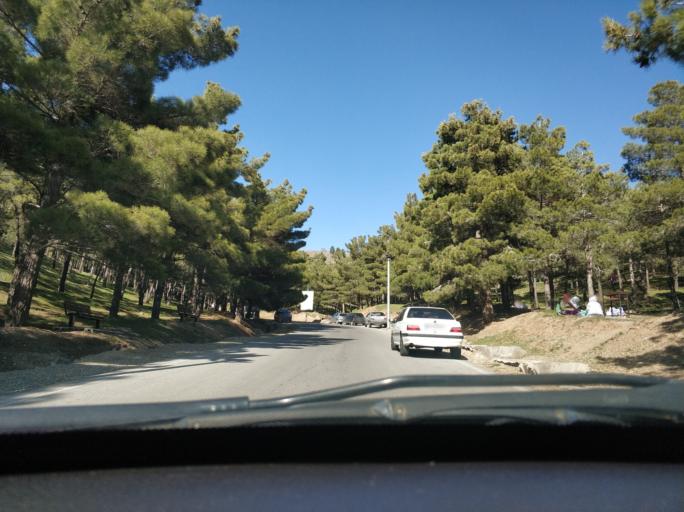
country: IR
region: Tehran
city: Tajrish
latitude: 35.7914
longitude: 51.5624
